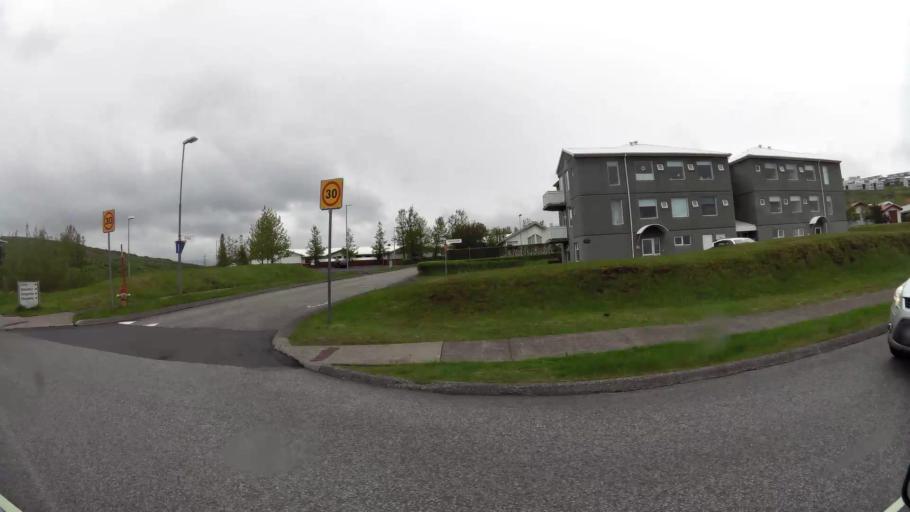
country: IS
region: Capital Region
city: Hafnarfjoerdur
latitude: 64.0588
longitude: -21.9266
